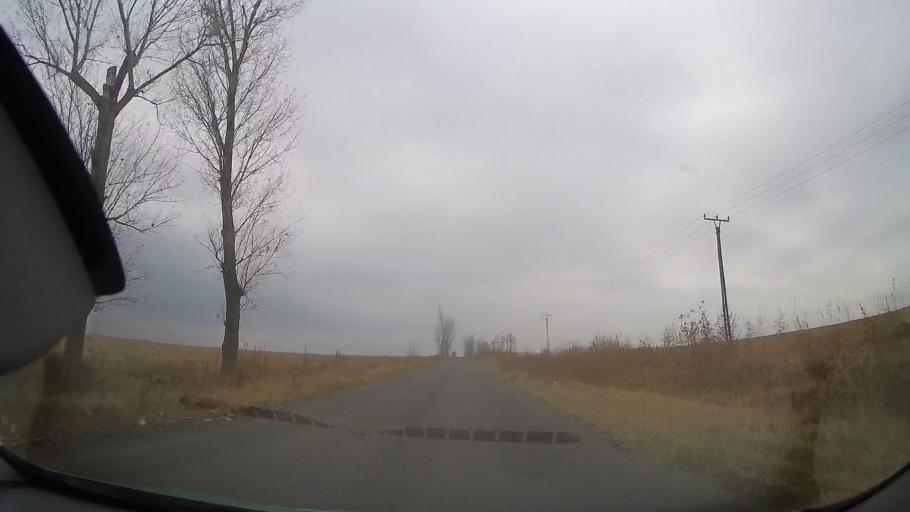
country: RO
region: Buzau
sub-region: Comuna Scutelnici
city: Scutelnici
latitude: 44.8829
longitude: 26.9523
